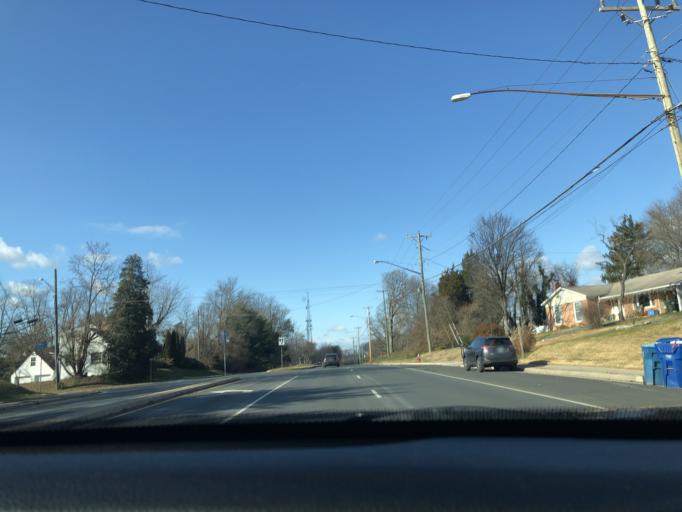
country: US
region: Virginia
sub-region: Fairfax County
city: Burke
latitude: 38.8208
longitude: -77.2779
